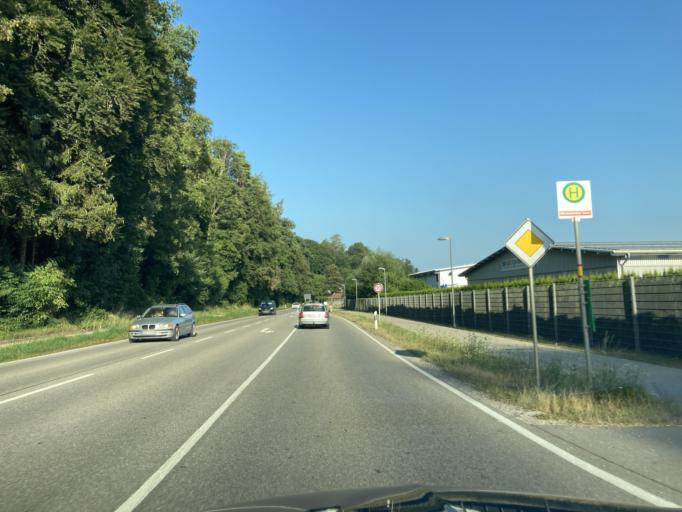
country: DE
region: Bavaria
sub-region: Upper Bavaria
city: Trostberg an der Alz
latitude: 48.0056
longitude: 12.5177
